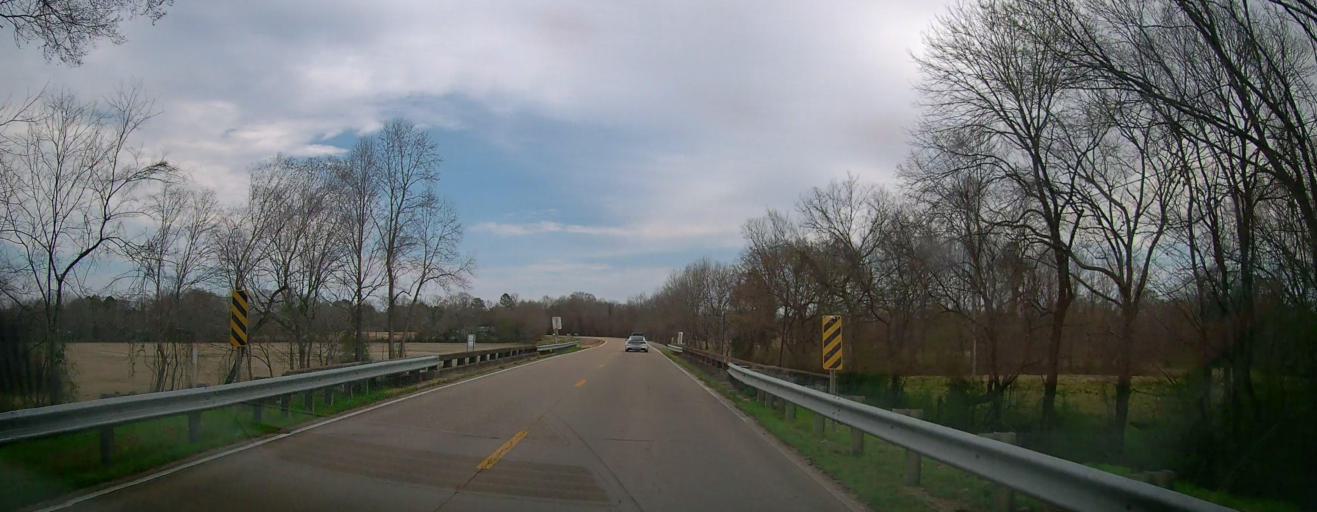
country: US
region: Mississippi
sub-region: Itawamba County
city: Fulton
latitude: 34.2521
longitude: -88.4742
